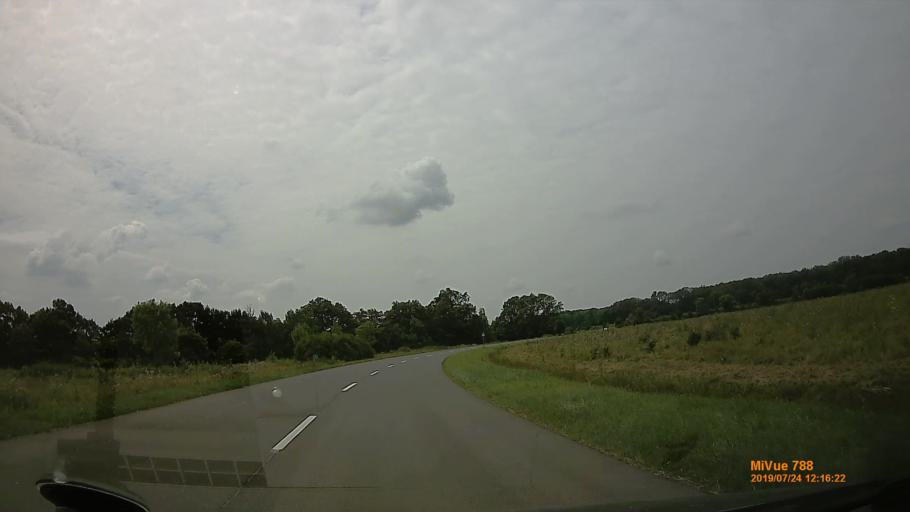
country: HU
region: Szabolcs-Szatmar-Bereg
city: Vasarosnameny
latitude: 48.1734
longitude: 22.3434
